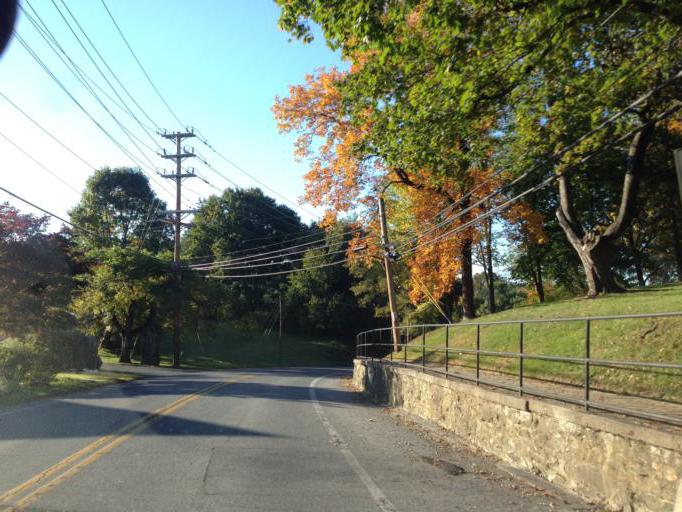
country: US
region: Maryland
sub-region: Carroll County
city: Sykesville
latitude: 39.3710
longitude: -76.9673
